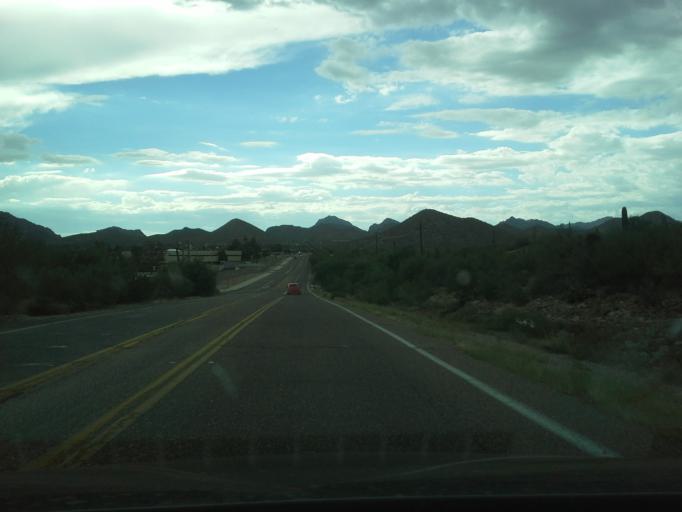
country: US
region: Arizona
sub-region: Pima County
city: South Tucson
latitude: 32.2070
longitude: -111.0062
